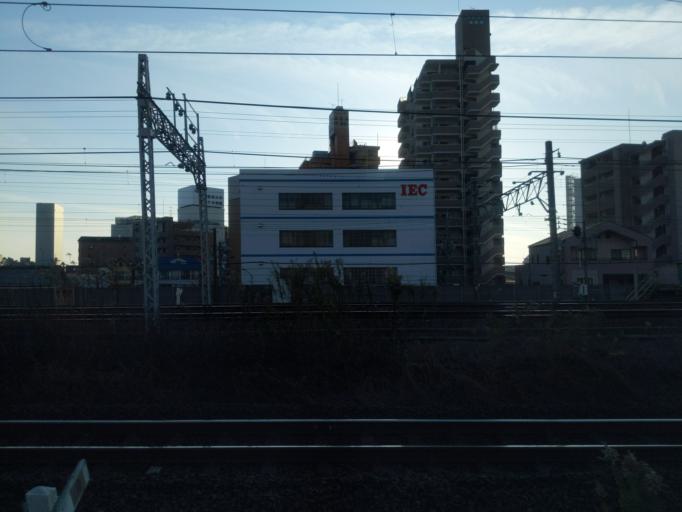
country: JP
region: Aichi
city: Nagoya-shi
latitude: 35.1466
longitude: 136.8921
